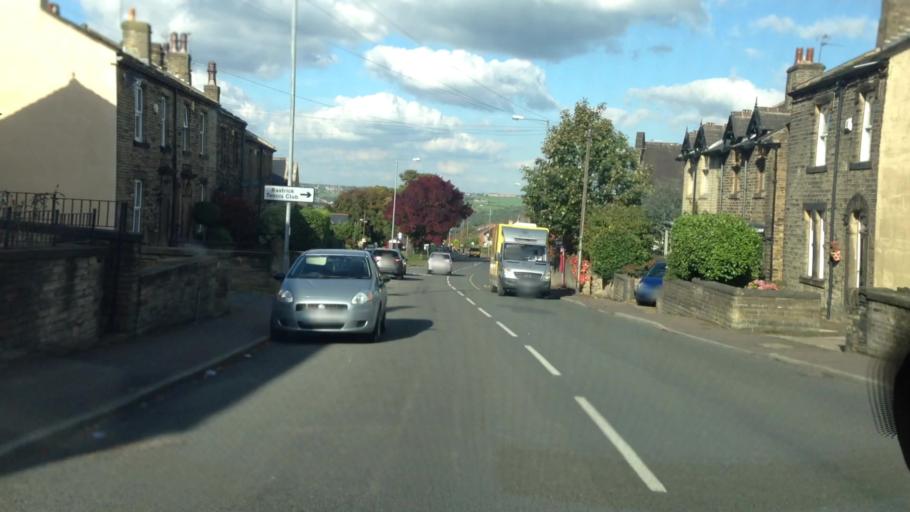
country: GB
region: England
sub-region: Calderdale
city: Brighouse
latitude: 53.6863
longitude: -1.7960
